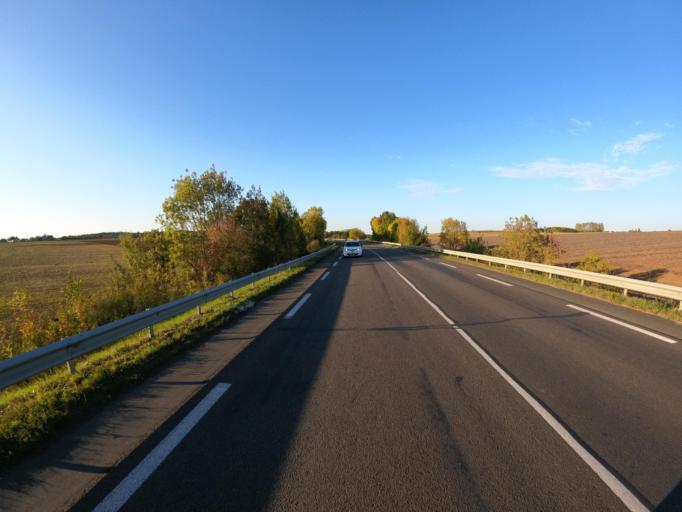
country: FR
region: Pays de la Loire
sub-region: Departement de la Vendee
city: Sainte-Hermine
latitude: 46.5643
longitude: -1.0469
